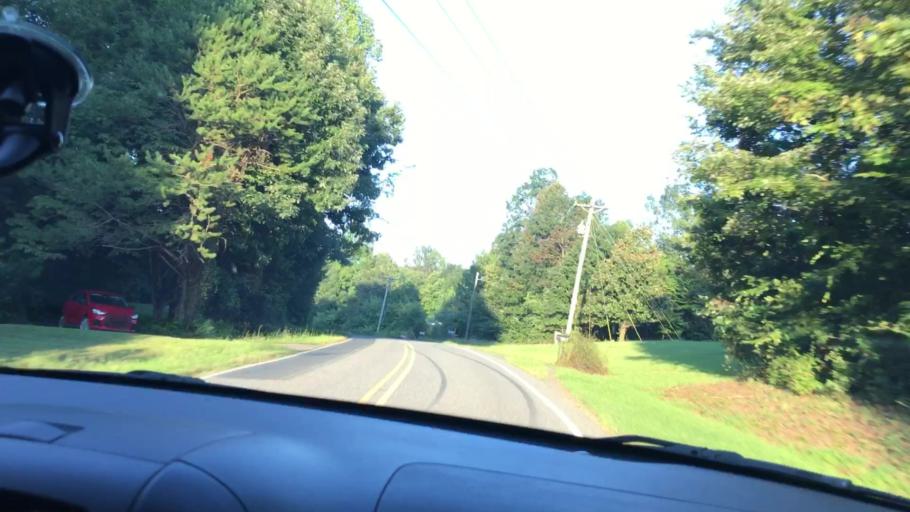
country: US
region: North Carolina
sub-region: Randolph County
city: Franklinville
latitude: 35.7998
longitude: -79.6602
